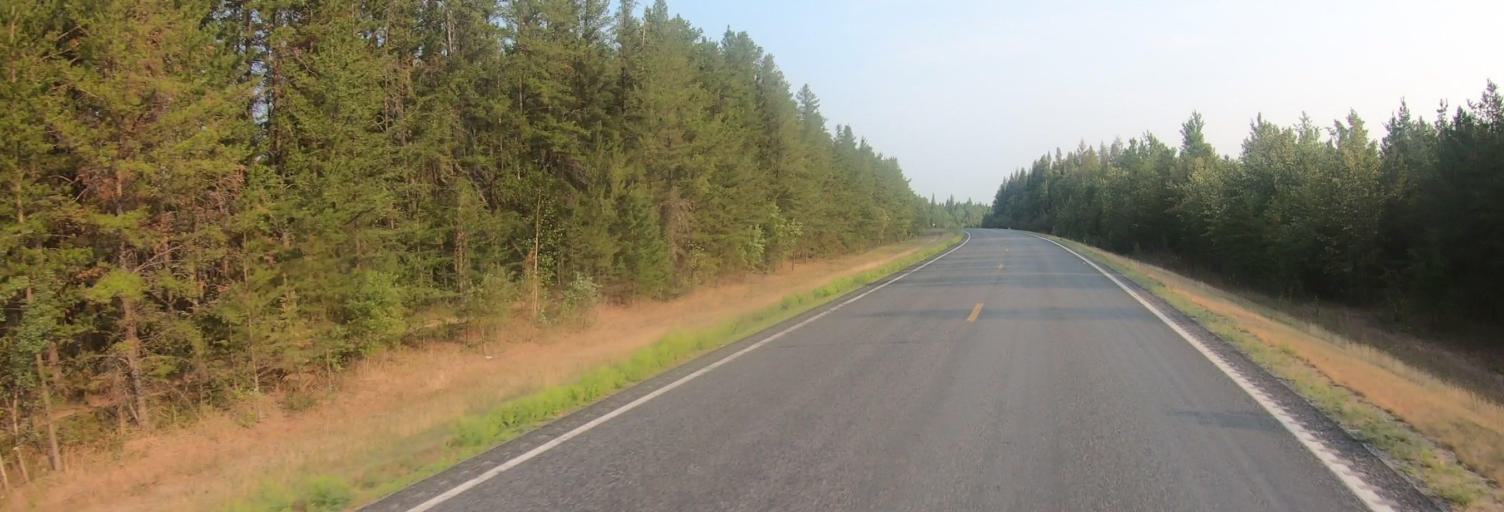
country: US
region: Minnesota
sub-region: Roseau County
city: Warroad
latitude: 48.7373
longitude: -95.3304
